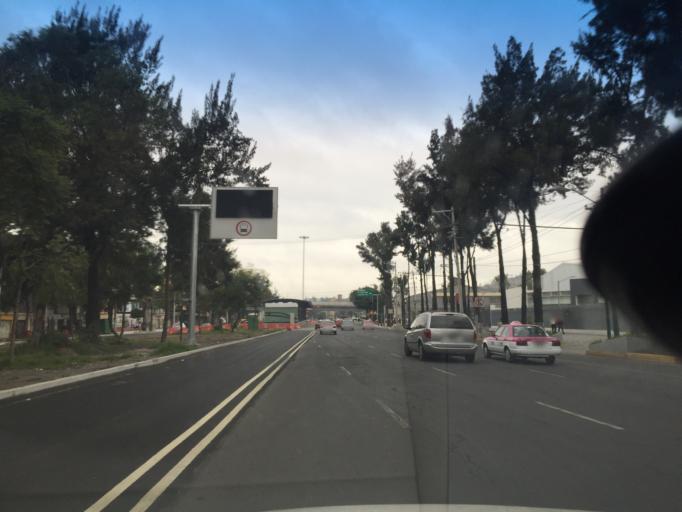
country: MX
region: Mexico City
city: Gustavo A. Madero
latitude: 19.4815
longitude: -99.1040
